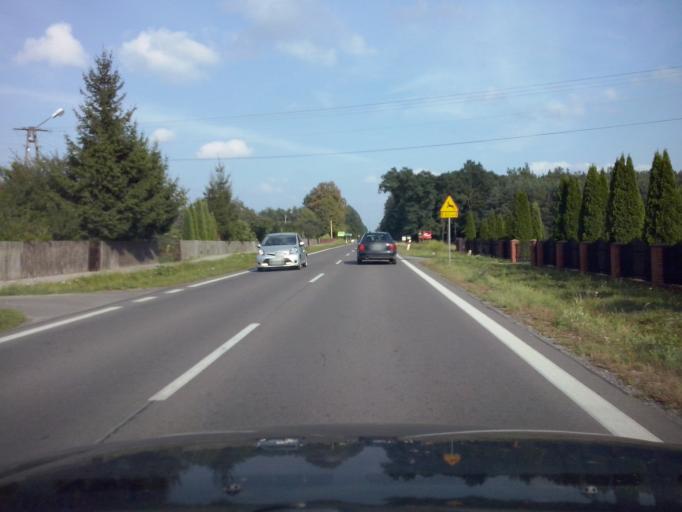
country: PL
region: Subcarpathian Voivodeship
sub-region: Powiat kolbuszowski
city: Niwiska
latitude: 50.2594
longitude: 21.6862
